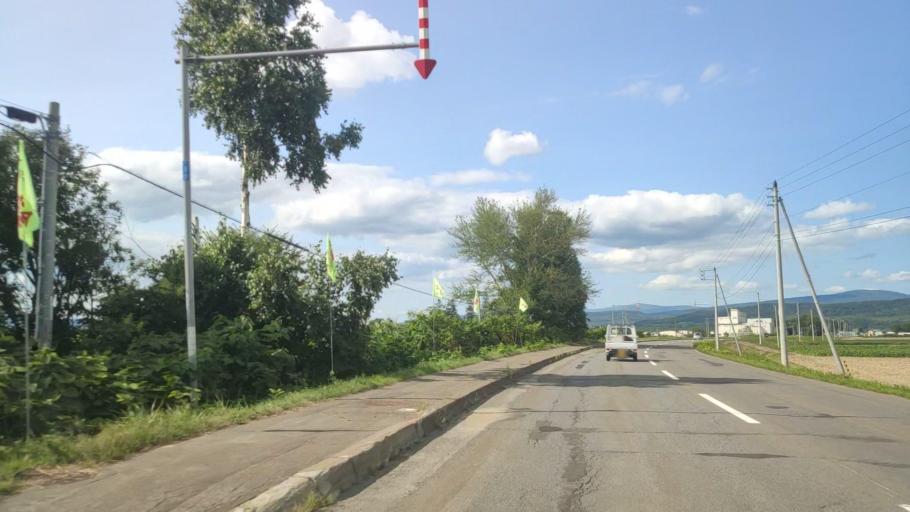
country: JP
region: Hokkaido
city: Nayoro
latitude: 44.4275
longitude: 142.3997
